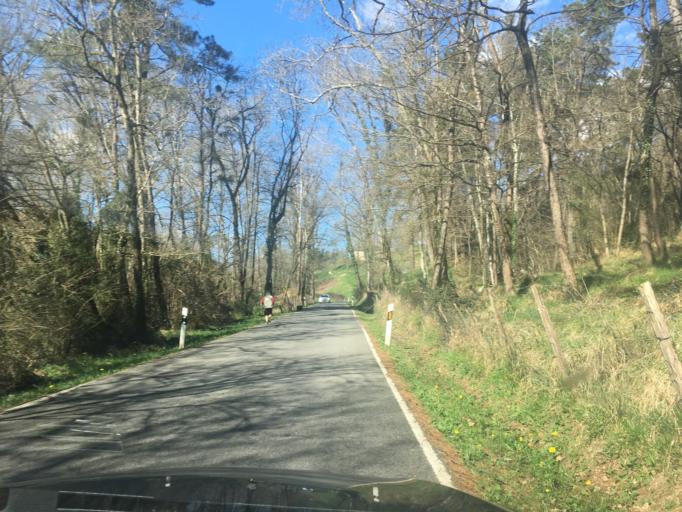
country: ES
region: Basque Country
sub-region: Bizkaia
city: Amorebieta
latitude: 43.2379
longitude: -2.7419
